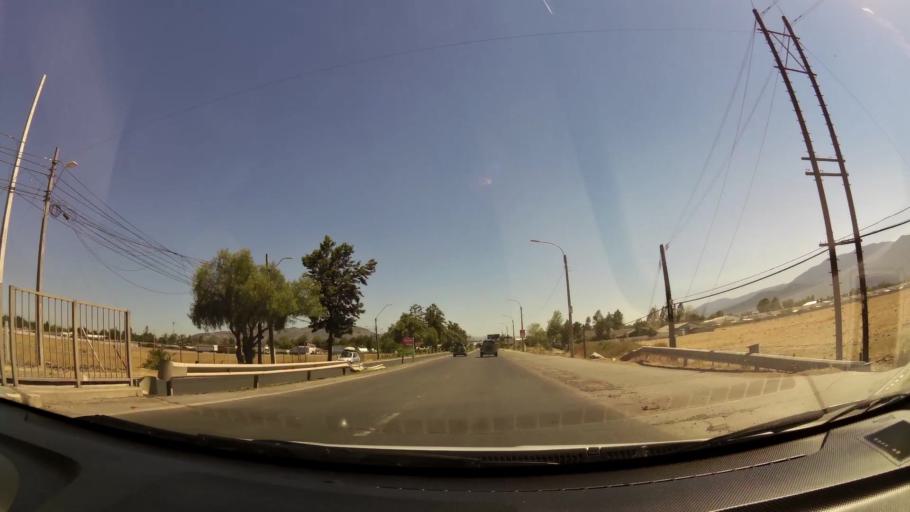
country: CL
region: O'Higgins
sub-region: Provincia de Colchagua
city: Chimbarongo
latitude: -34.5805
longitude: -70.9795
